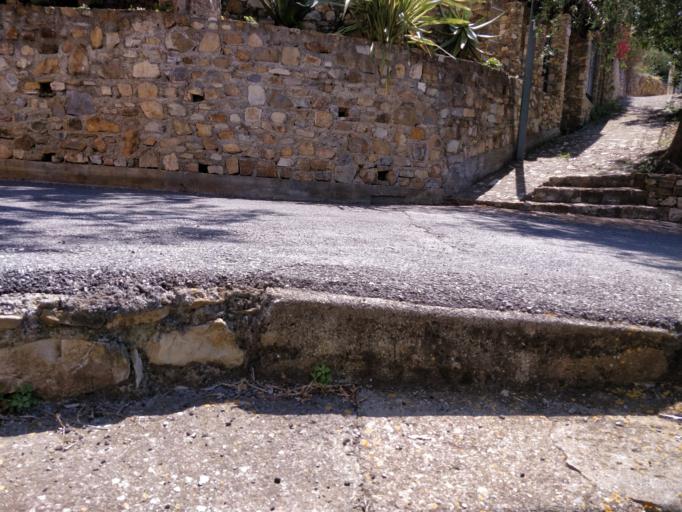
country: IT
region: Liguria
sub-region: Provincia di Savona
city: Marina di Andora
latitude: 43.9573
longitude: 8.1527
